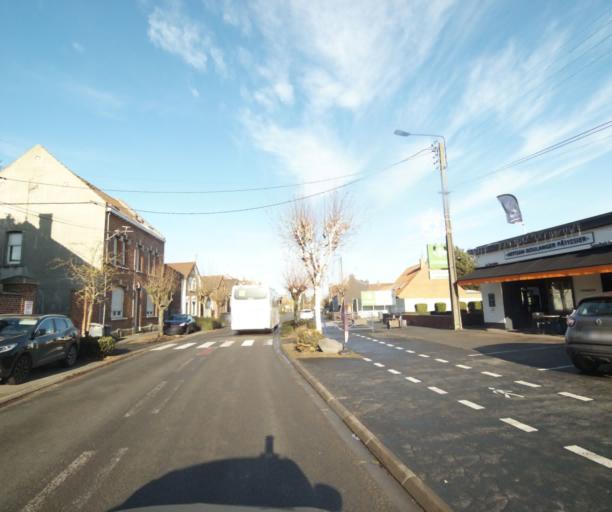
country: FR
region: Nord-Pas-de-Calais
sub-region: Departement du Nord
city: Famars
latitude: 50.3200
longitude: 3.5183
